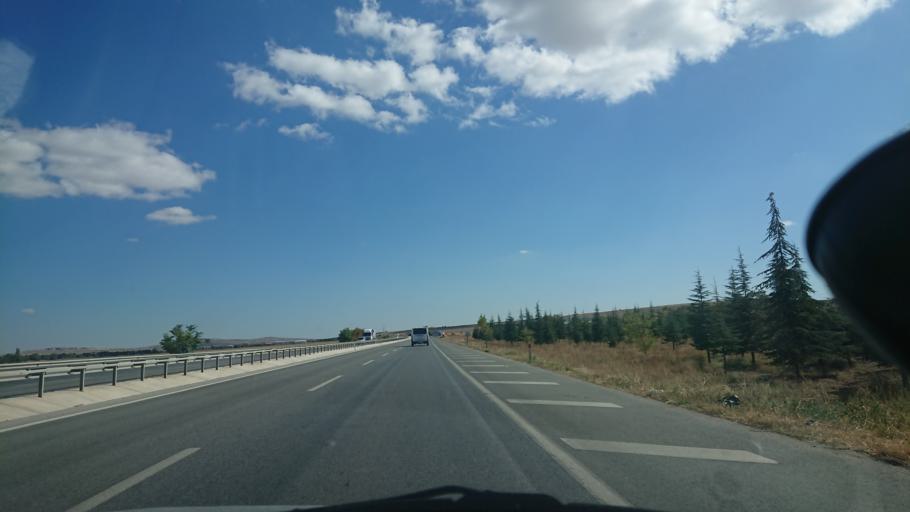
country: TR
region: Eskisehir
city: Mahmudiye
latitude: 39.5358
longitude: 30.9447
